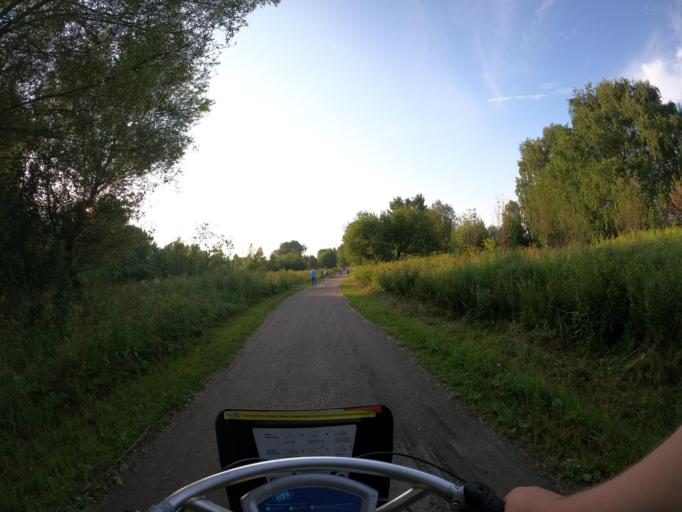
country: RU
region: Moscow
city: Strogino
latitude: 55.8198
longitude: 37.4106
